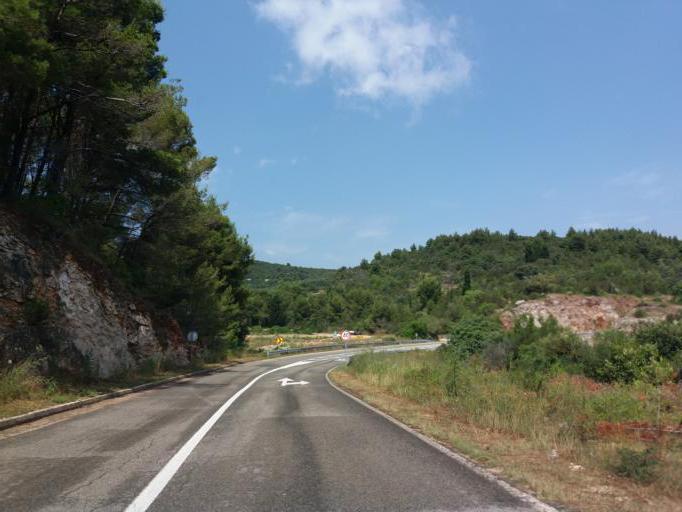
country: HR
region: Zadarska
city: Sali
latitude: 43.9616
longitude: 15.1122
